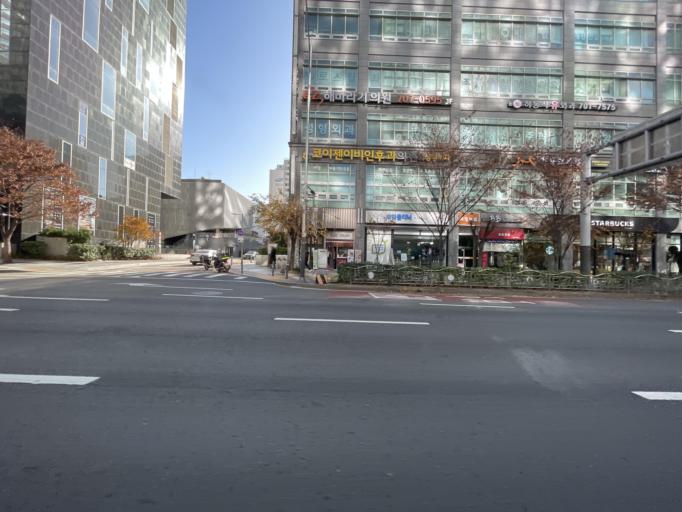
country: KR
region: Seoul
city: Seoul
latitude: 37.5417
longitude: 126.9491
